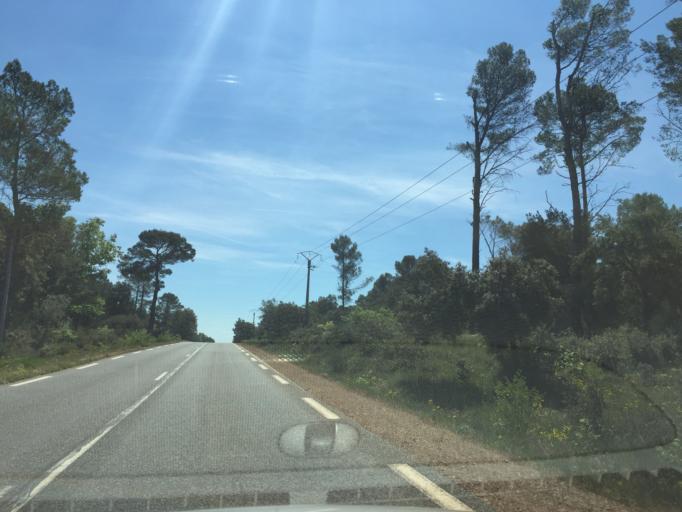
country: FR
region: Provence-Alpes-Cote d'Azur
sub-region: Departement du Var
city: Lorgues
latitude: 43.5227
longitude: 6.3306
